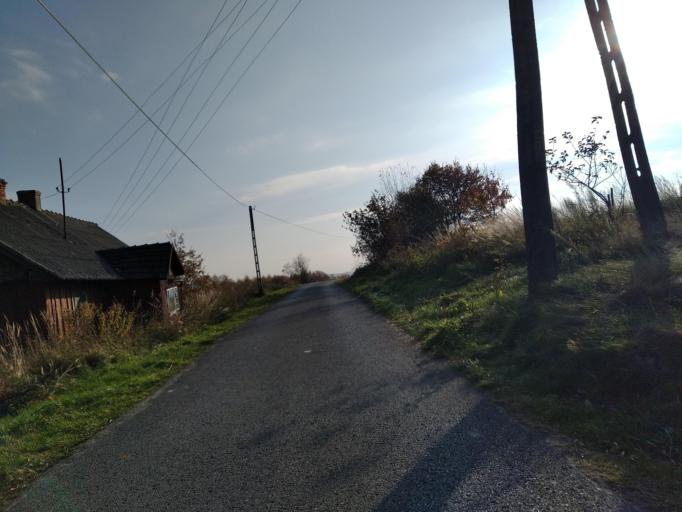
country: PL
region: Subcarpathian Voivodeship
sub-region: Powiat strzyzowski
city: Babica
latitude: 49.9043
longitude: 21.8541
